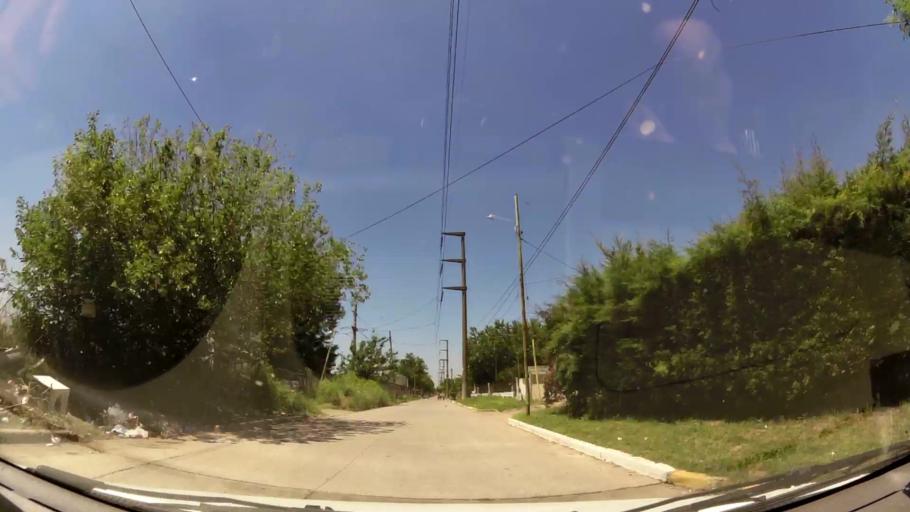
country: AR
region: Buenos Aires
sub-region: Partido de Merlo
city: Merlo
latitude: -34.6529
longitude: -58.7072
